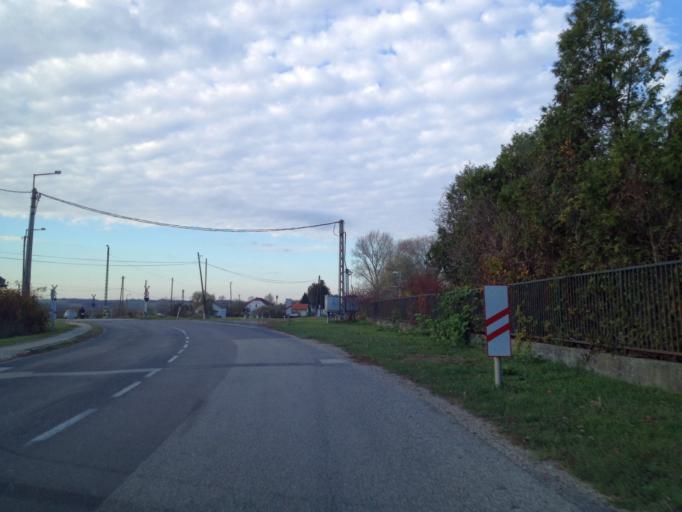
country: HU
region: Gyor-Moson-Sopron
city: Bakonyszentlaszlo
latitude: 47.4397
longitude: 17.8210
